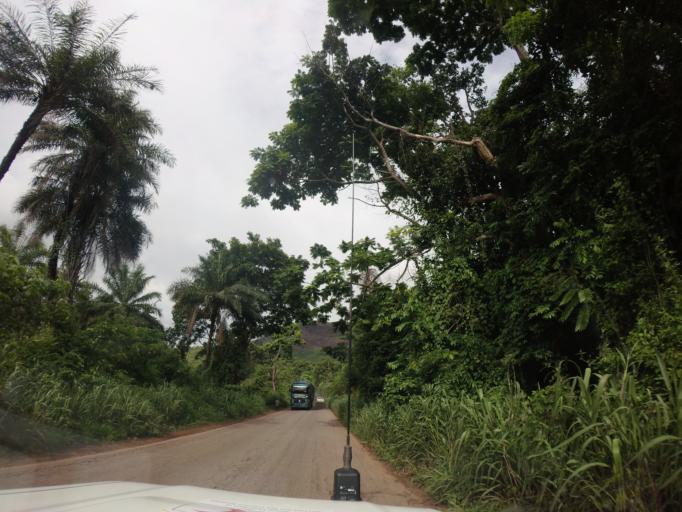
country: GN
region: Kindia
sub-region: Coyah
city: Coyah
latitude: 9.7374
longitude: -13.3719
